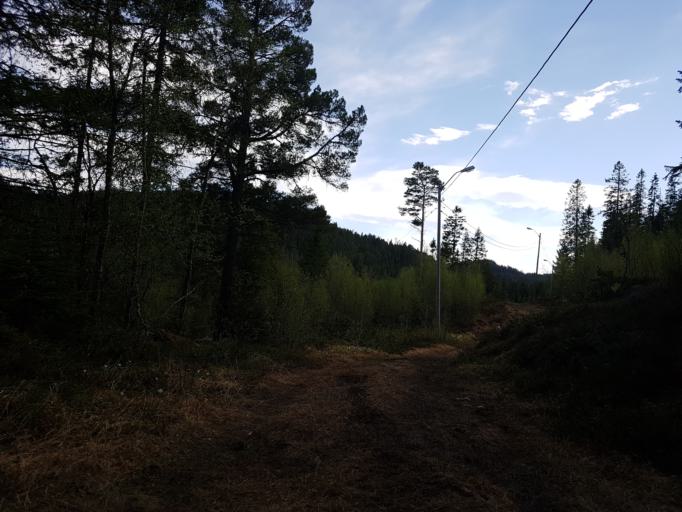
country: NO
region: Sor-Trondelag
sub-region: Trondheim
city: Trondheim
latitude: 63.4445
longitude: 10.2928
